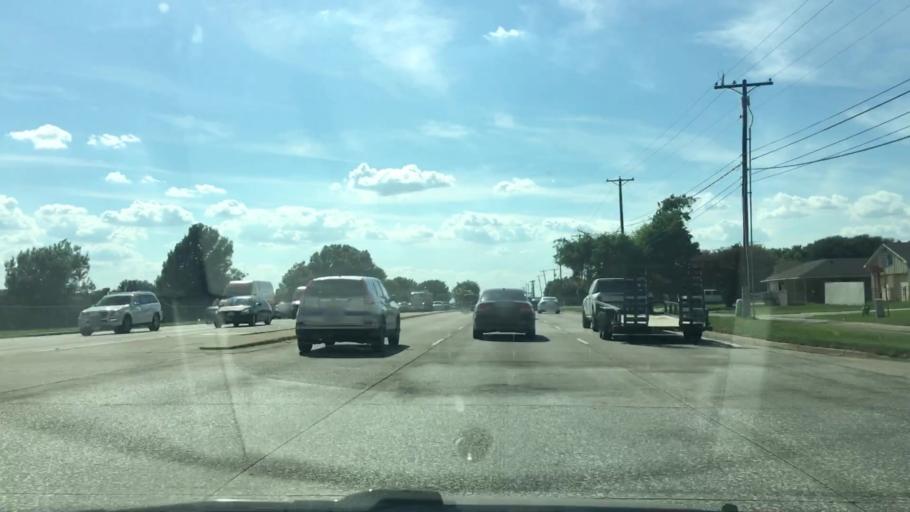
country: US
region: Texas
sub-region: Collin County
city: McKinney
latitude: 33.2170
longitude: -96.6458
